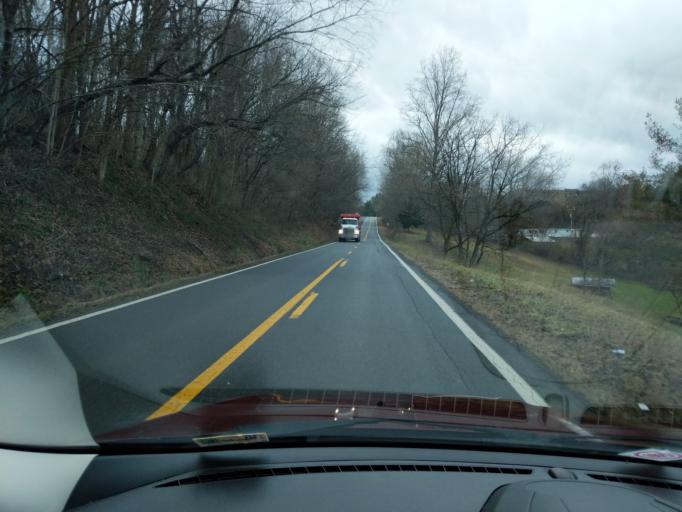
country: US
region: West Virginia
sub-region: Greenbrier County
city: Alderson
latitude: 37.7348
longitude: -80.6273
